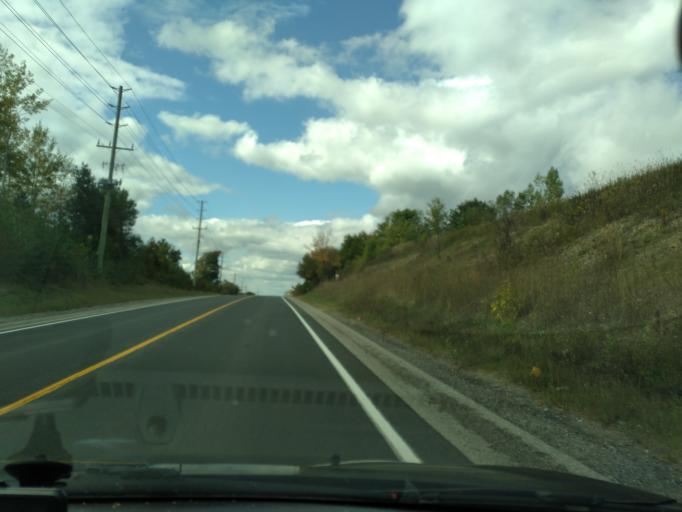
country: CA
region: Ontario
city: Innisfil
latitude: 44.2632
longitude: -79.7566
